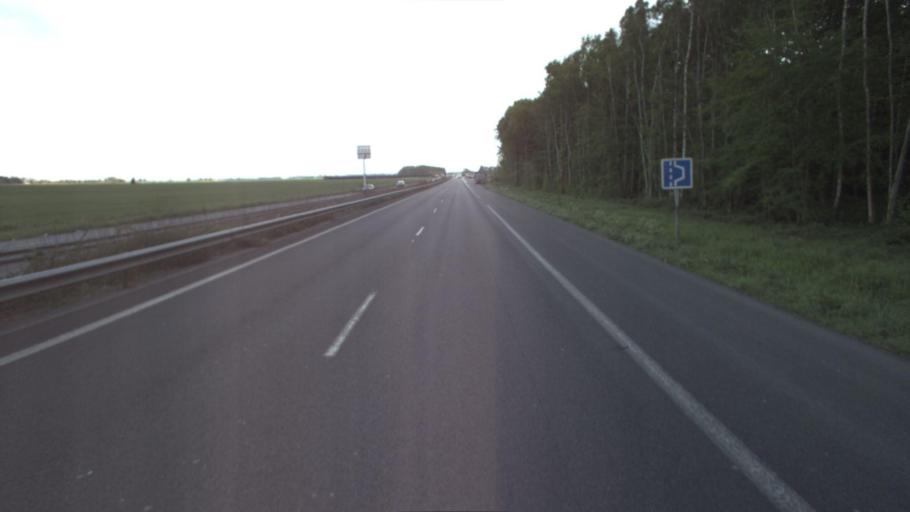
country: FR
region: Ile-de-France
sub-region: Departement de Seine-et-Marne
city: Fontenay-Tresigny
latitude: 48.6941
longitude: 2.9094
